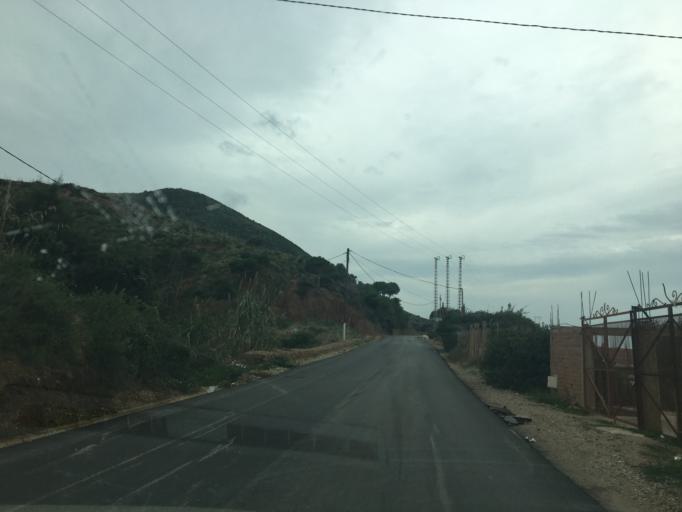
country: DZ
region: Tipaza
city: Tipasa
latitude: 36.6395
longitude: 2.3357
